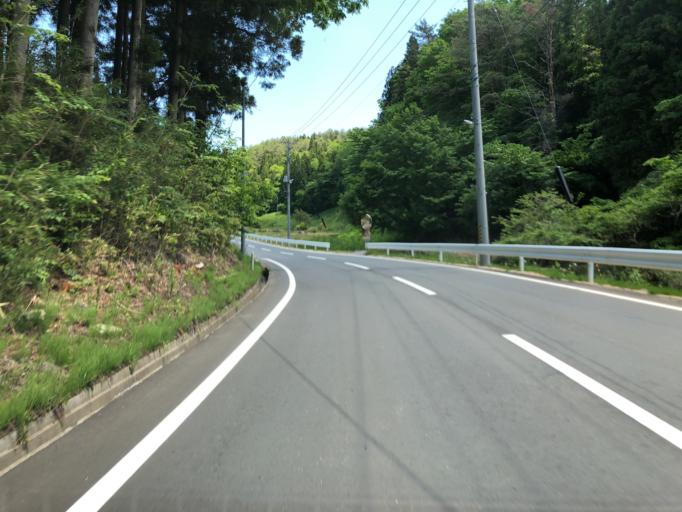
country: JP
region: Fukushima
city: Funehikimachi-funehiki
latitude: 37.5125
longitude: 140.6809
